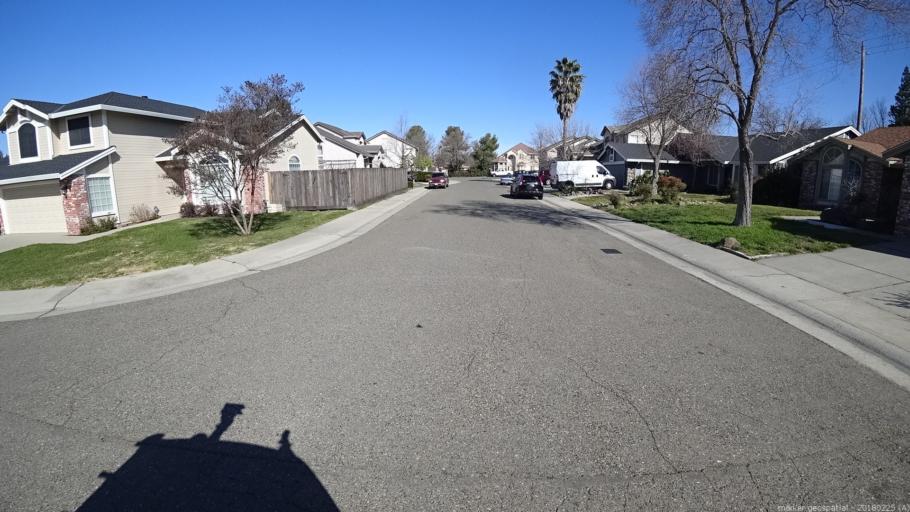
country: US
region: California
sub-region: Sacramento County
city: North Highlands
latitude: 38.7234
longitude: -121.3932
